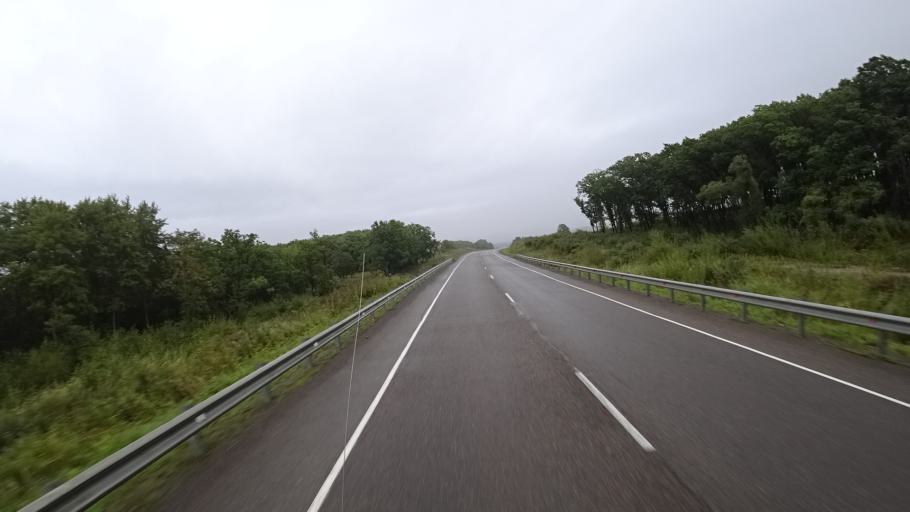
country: RU
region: Primorskiy
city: Monastyrishche
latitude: 44.2737
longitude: 132.4729
